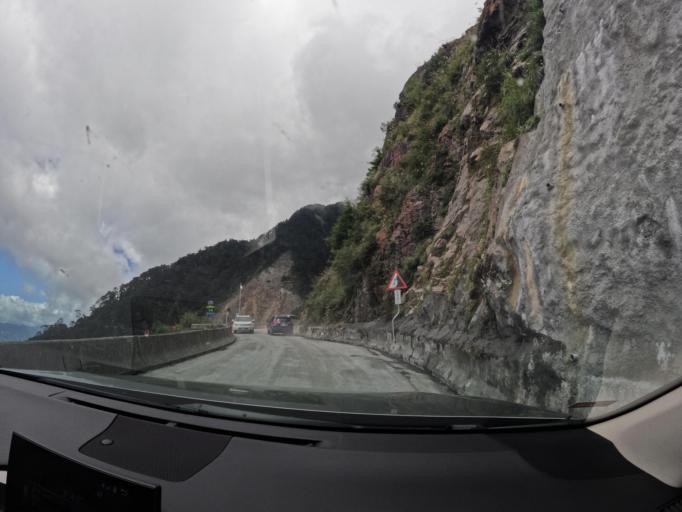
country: TW
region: Taiwan
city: Yujing
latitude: 23.2665
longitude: 120.9524
